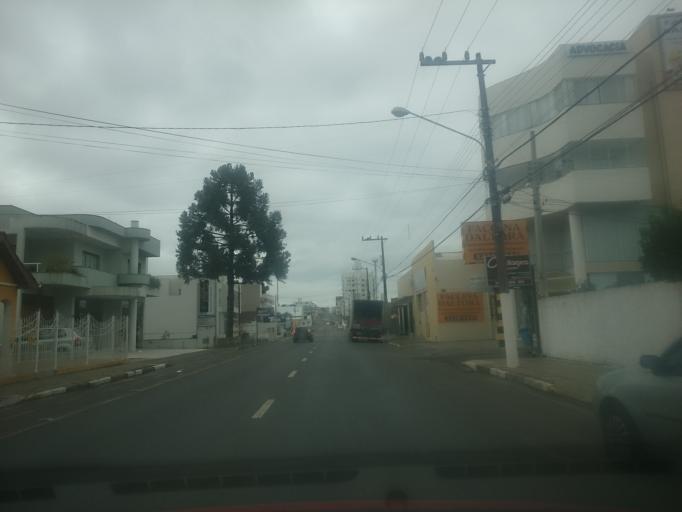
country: BR
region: Santa Catarina
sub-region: Lages
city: Lages
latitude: -27.8076
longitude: -50.3116
